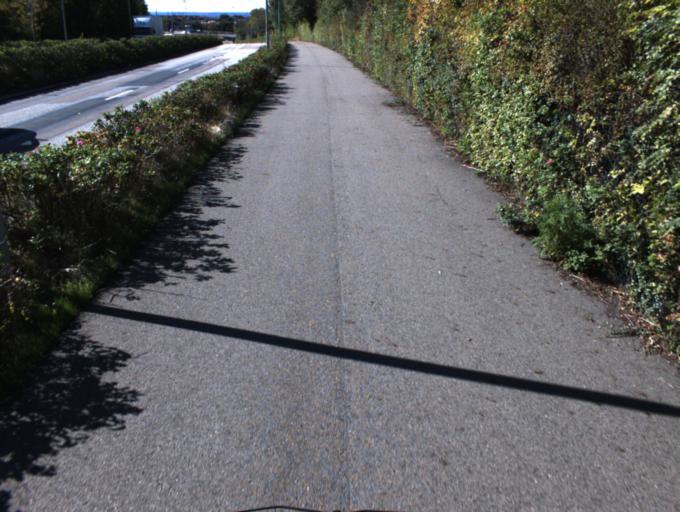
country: SE
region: Skane
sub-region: Helsingborg
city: Helsingborg
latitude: 56.0256
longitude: 12.7334
